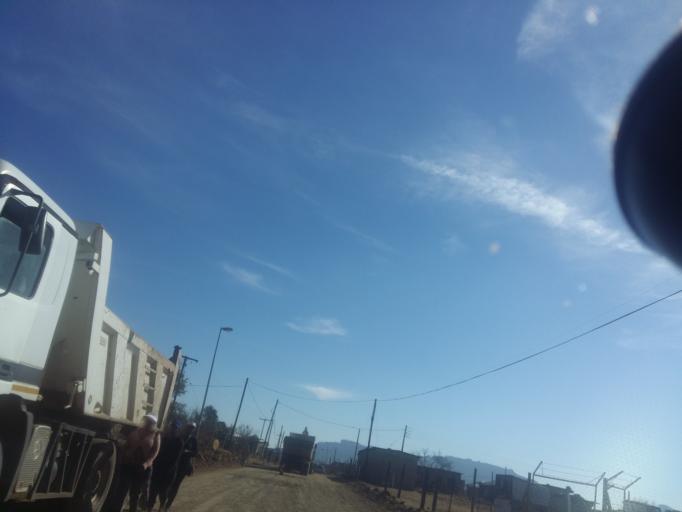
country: LS
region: Maseru
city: Maseru
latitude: -29.3707
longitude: 27.5287
